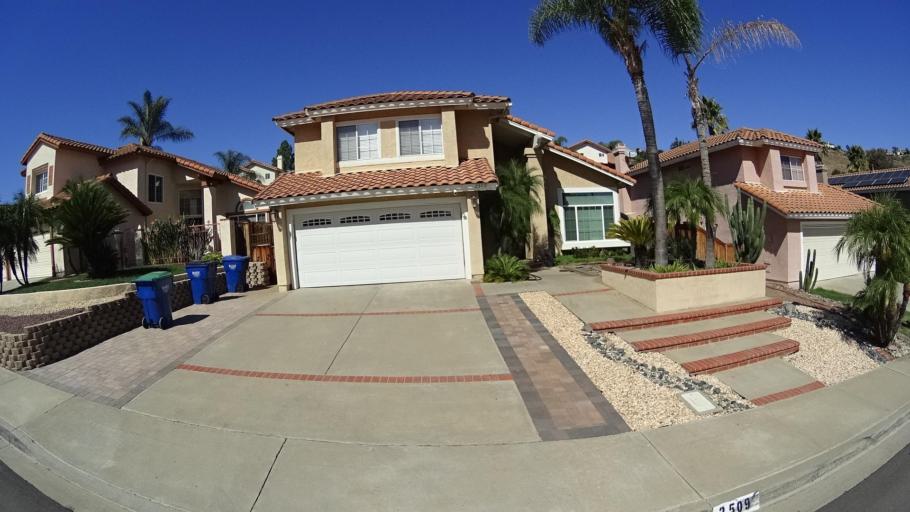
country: US
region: California
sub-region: San Diego County
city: Rancho San Diego
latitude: 32.7453
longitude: -116.9187
